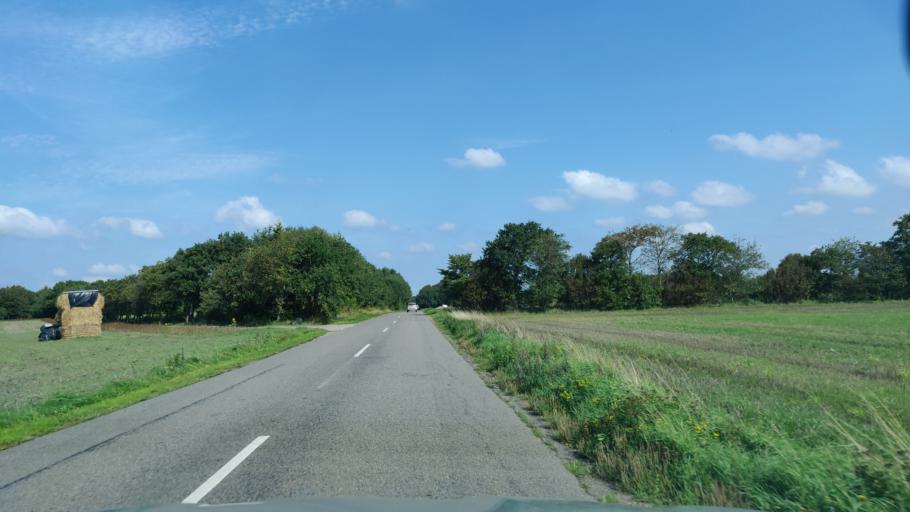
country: DK
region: Central Jutland
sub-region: Herning Kommune
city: Avlum
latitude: 56.2274
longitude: 8.8637
